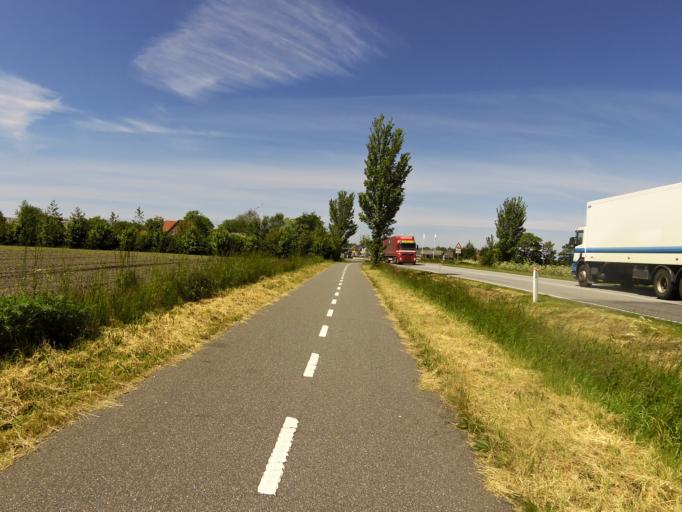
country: DK
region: South Denmark
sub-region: Haderslev Kommune
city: Gram
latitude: 55.2811
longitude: 9.0630
